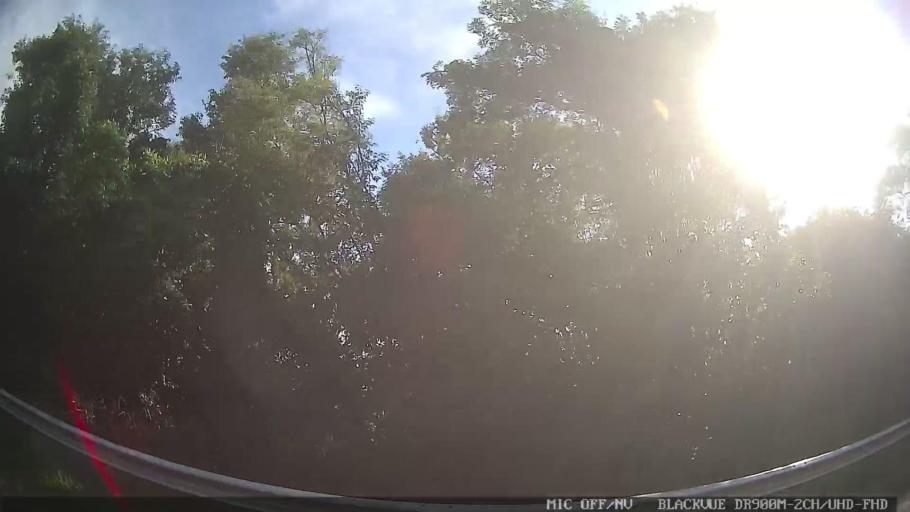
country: BR
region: Sao Paulo
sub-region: Tiete
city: Tiete
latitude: -23.1144
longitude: -47.7404
